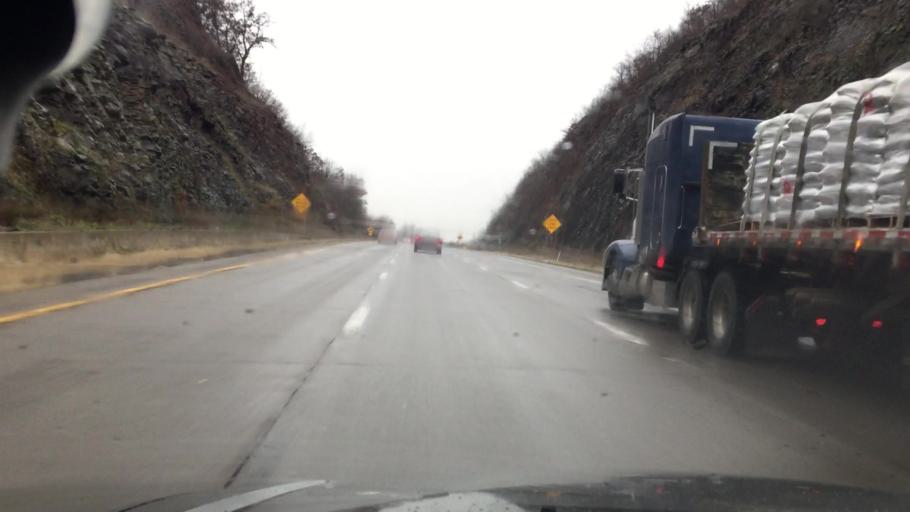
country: US
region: Pennsylvania
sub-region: Luzerne County
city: Ashley
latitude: 41.1732
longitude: -75.9455
